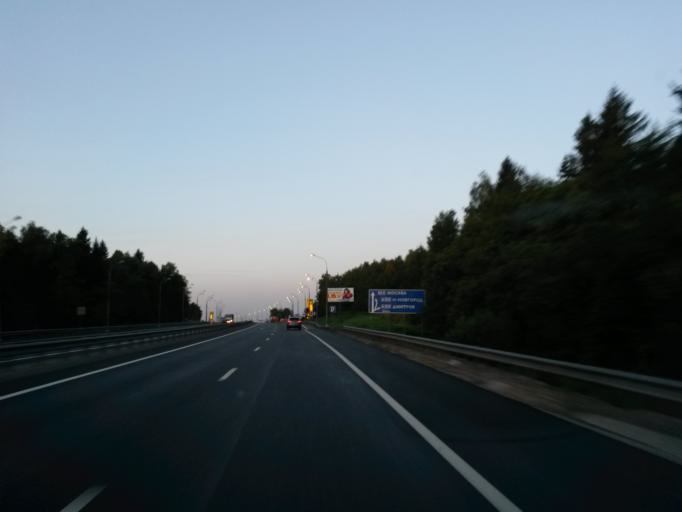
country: RU
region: Moskovskaya
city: Svatkovo
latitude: 56.3460
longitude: 38.2684
